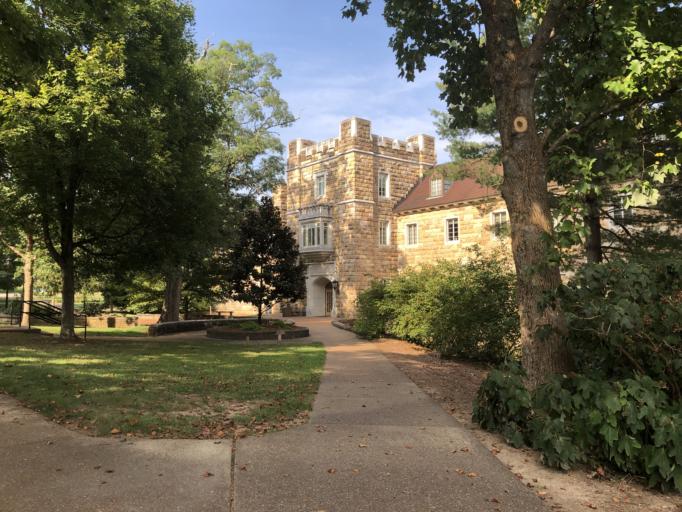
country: US
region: Tennessee
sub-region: Franklin County
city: Sewanee
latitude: 35.2039
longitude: -85.9195
